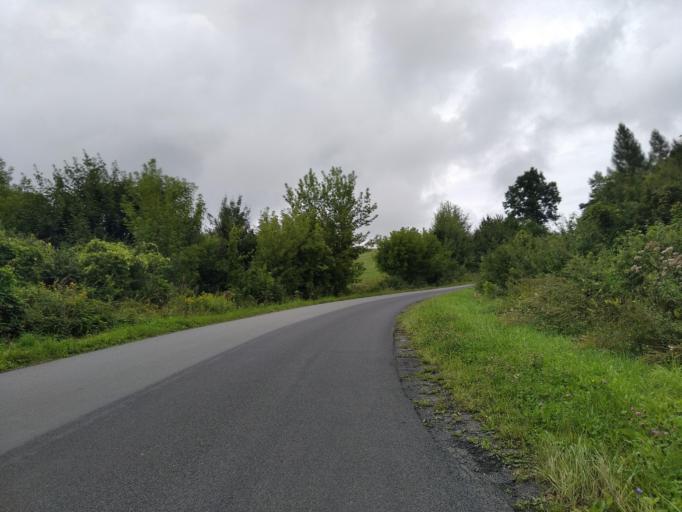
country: PL
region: Subcarpathian Voivodeship
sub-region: Powiat rzeszowski
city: Dynow
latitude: 49.7275
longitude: 22.2970
